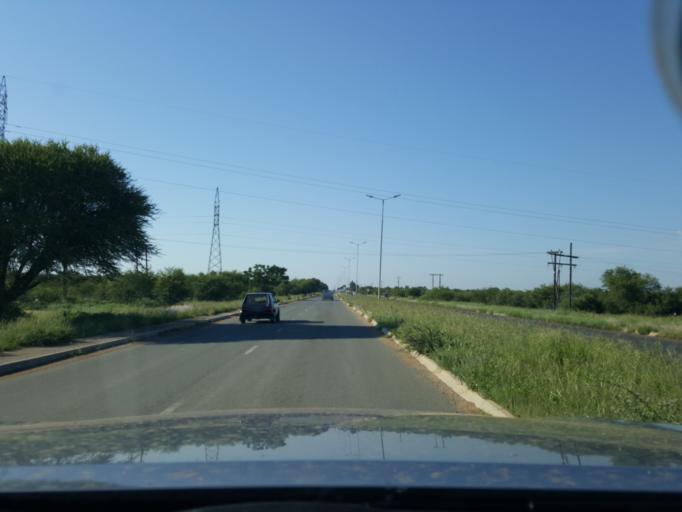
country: ZA
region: North-West
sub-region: Ngaka Modiri Molema District Municipality
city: Mmabatho
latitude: -25.8063
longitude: 25.6323
